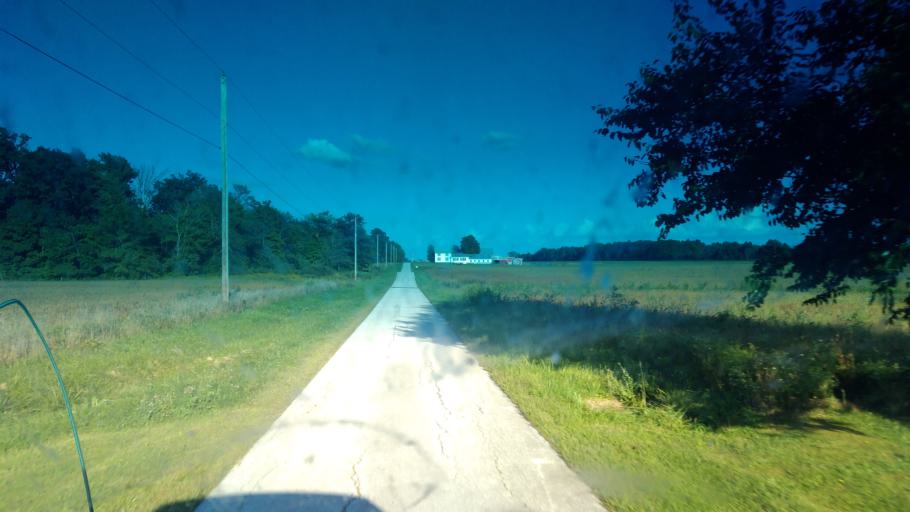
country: US
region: Ohio
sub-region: Wyandot County
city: Carey
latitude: 40.9412
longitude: -83.4645
